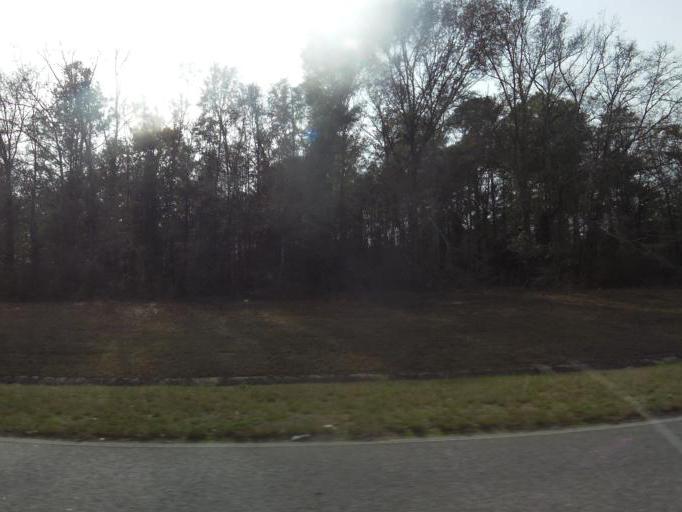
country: US
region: Alabama
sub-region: Houston County
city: Dothan
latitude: 31.2096
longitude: -85.3548
